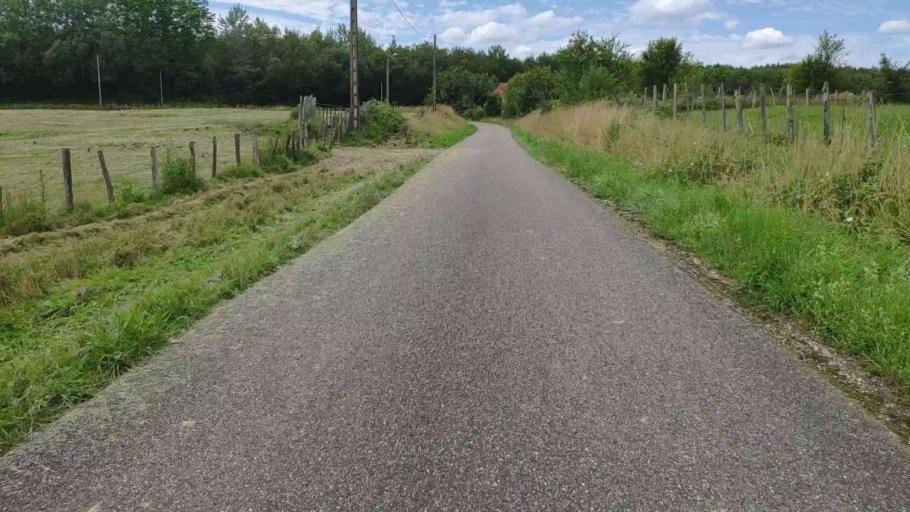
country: FR
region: Franche-Comte
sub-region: Departement du Jura
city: Chaussin
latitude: 46.8873
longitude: 5.4466
